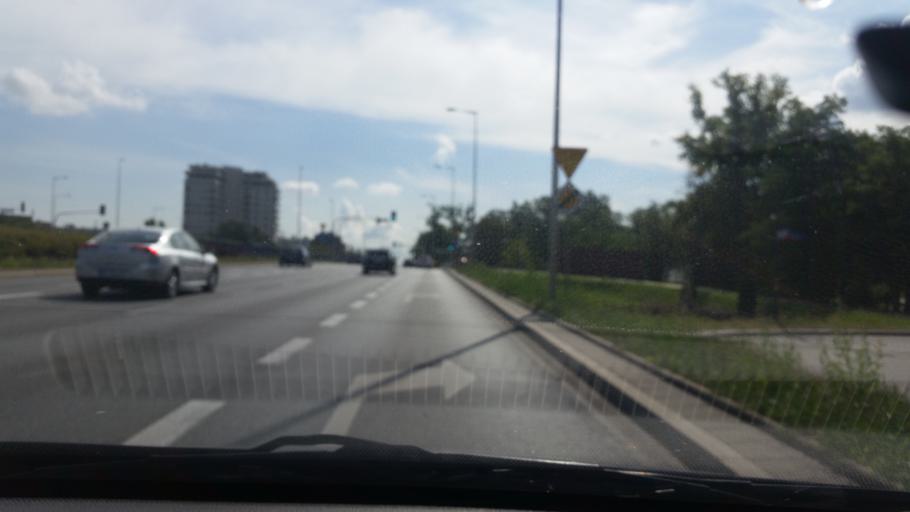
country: PL
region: Masovian Voivodeship
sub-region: Warszawa
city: Bielany
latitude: 52.2629
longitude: 20.9516
